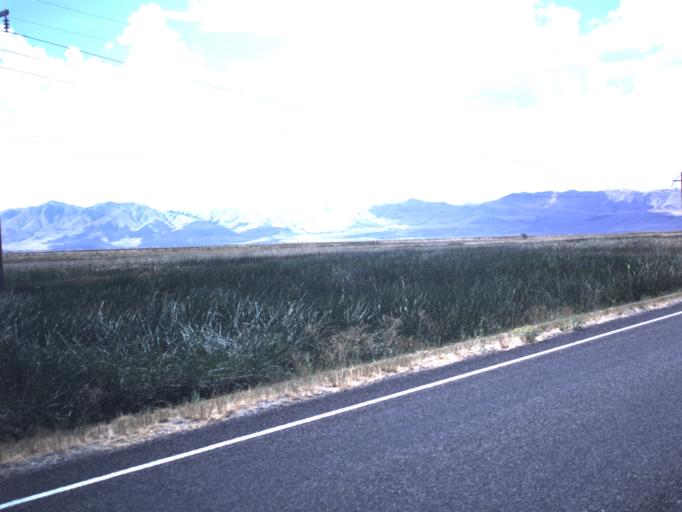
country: US
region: Utah
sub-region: Box Elder County
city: Tremonton
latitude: 41.6115
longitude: -112.3551
